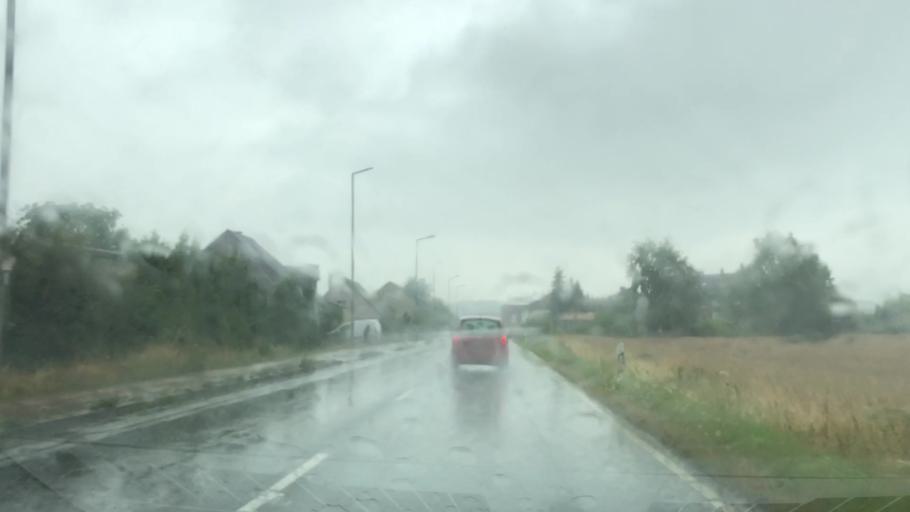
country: DE
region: North Rhine-Westphalia
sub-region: Regierungsbezirk Detmold
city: Minden
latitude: 52.2745
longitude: 8.9675
